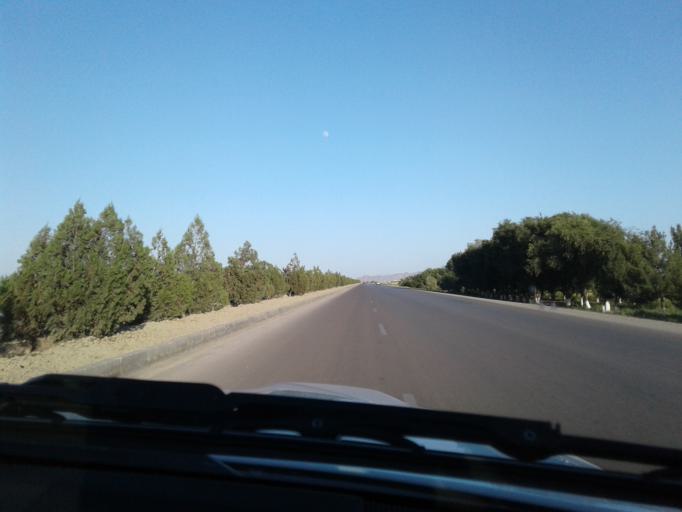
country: TM
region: Ahal
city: Baharly
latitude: 38.3399
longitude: 57.5651
